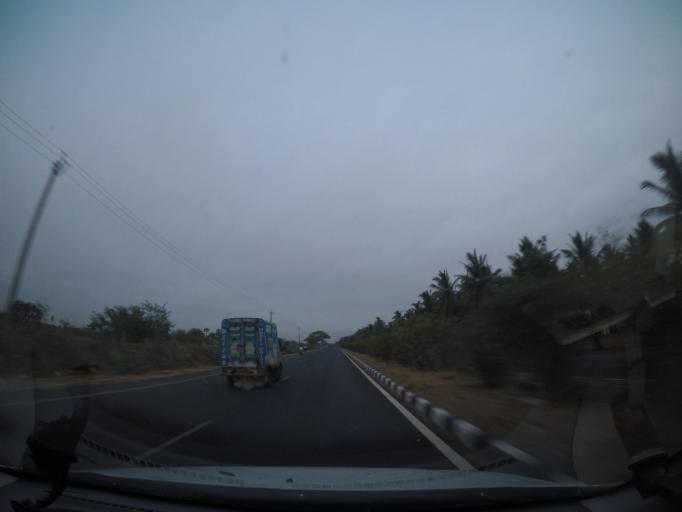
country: IN
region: Andhra Pradesh
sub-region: West Godavari
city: Tadepallegudem
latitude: 16.8072
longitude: 81.3135
